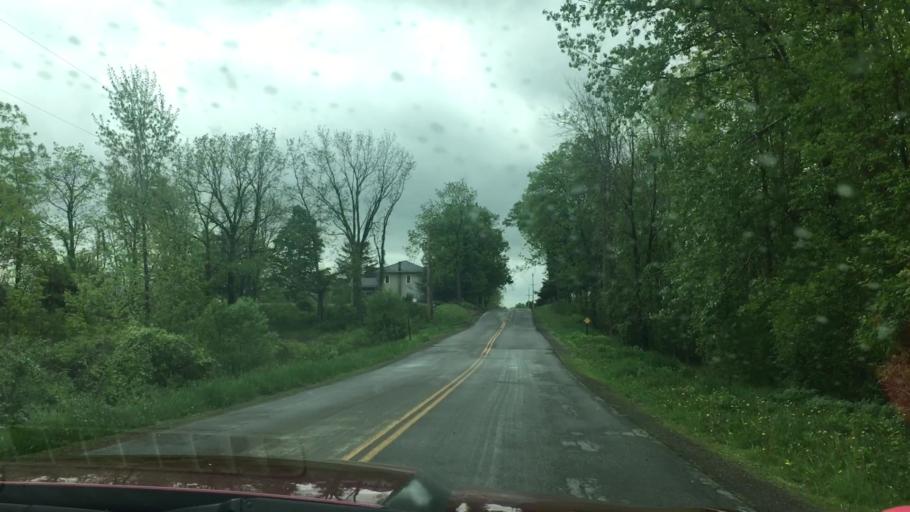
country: US
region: New York
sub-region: Genesee County
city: Batavia
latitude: 43.0820
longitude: -78.1395
